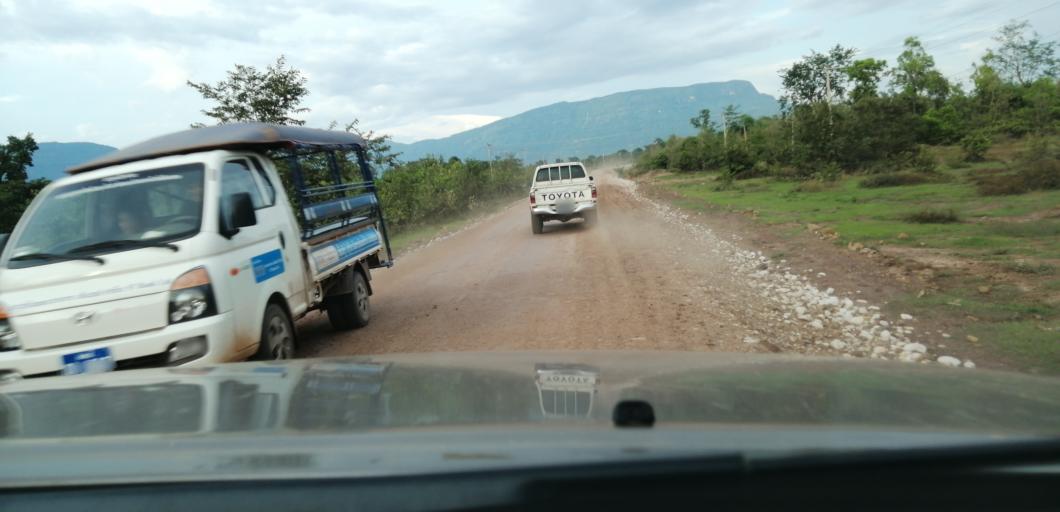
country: LA
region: Attapu
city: Attapu
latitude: 14.7095
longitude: 106.4829
